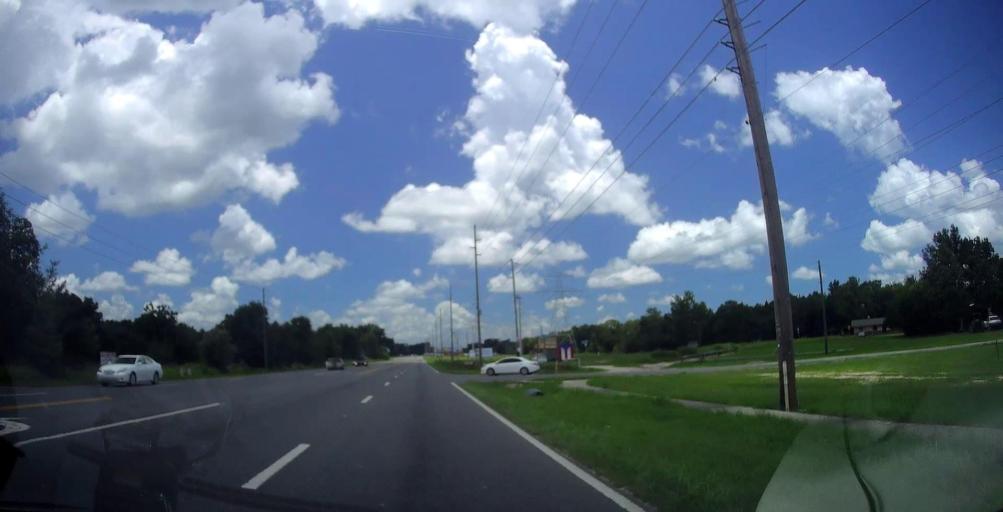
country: US
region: Florida
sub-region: Marion County
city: Silver Springs Shores
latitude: 29.1311
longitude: -82.0409
